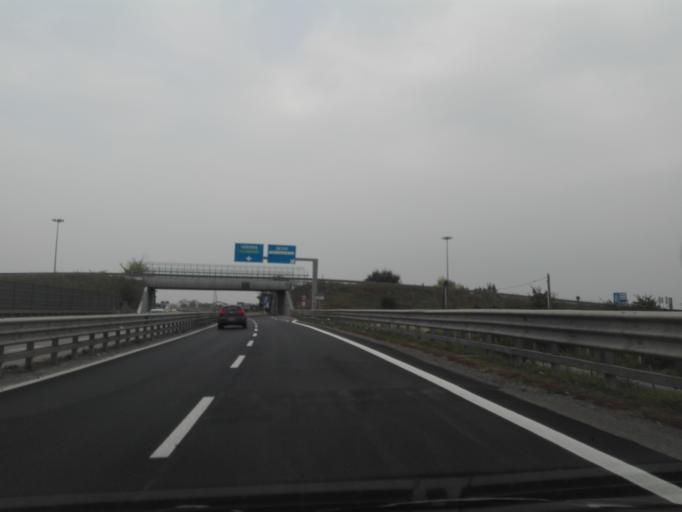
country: IT
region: Veneto
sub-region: Provincia di Verona
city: Campagnola
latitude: 45.3656
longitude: 11.0588
